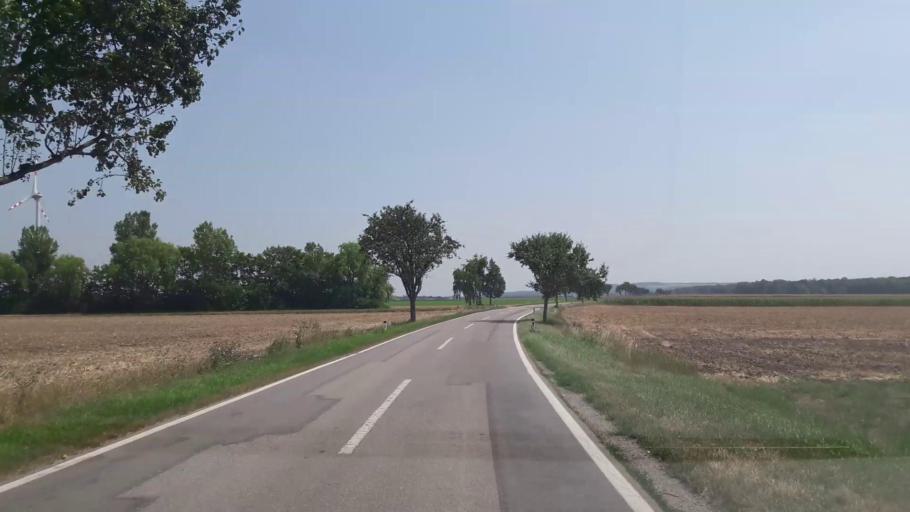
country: AT
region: Lower Austria
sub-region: Politischer Bezirk Bruck an der Leitha
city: Sommerein
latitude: 48.0204
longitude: 16.6872
